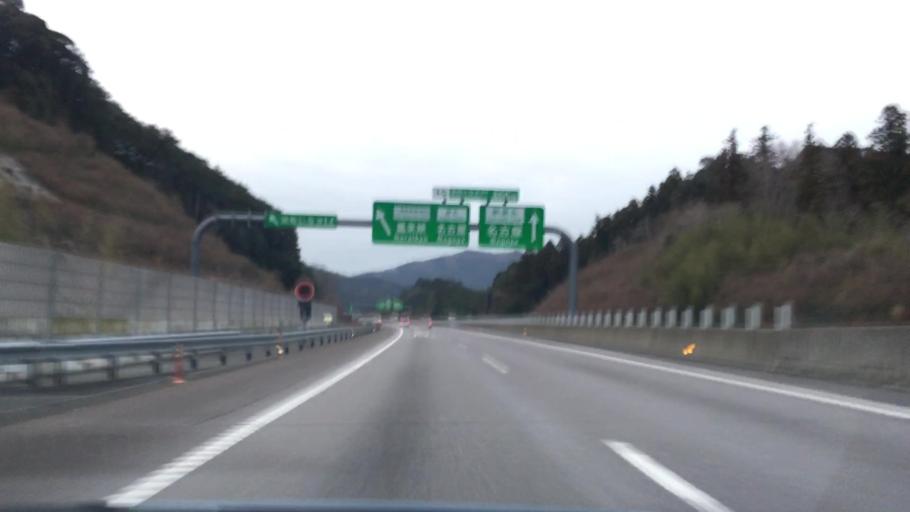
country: JP
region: Shizuoka
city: Hamakita
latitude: 34.8830
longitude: 137.6589
